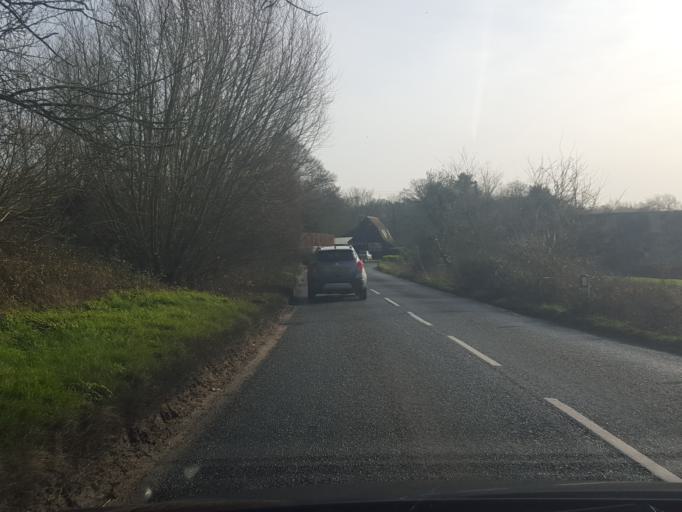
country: GB
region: England
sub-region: Suffolk
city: Sudbury
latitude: 51.9886
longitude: 0.7734
